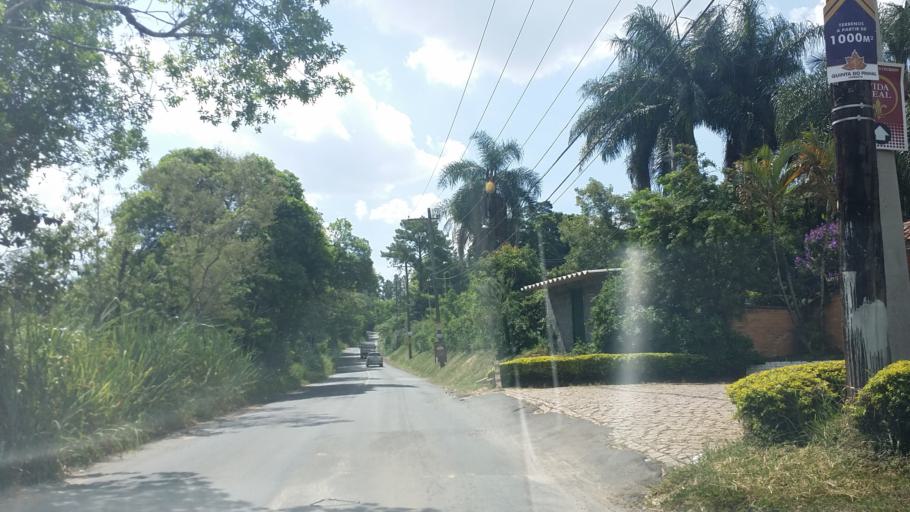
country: BR
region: Sao Paulo
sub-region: Itupeva
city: Itupeva
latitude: -23.1913
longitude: -47.0271
